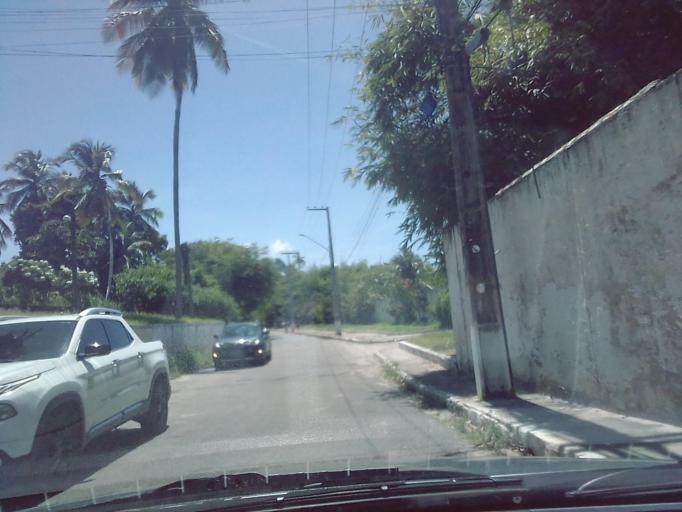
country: BR
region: Pernambuco
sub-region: Igarassu
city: Igarassu
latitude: -7.8446
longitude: -34.8443
